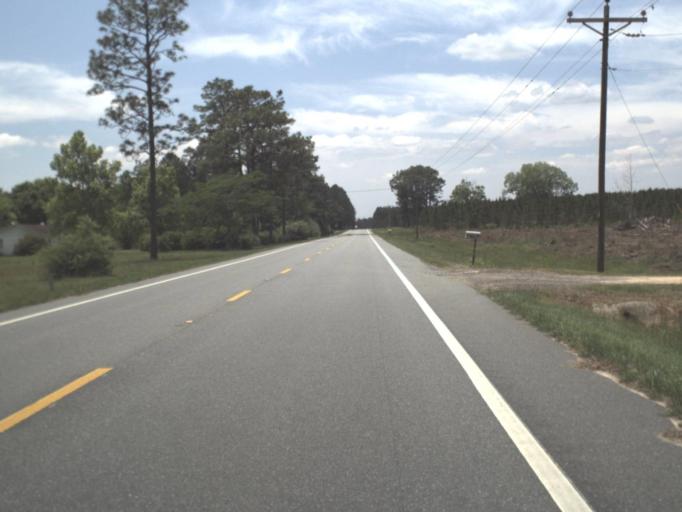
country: US
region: Florida
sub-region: Gulf County
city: Wewahitchka
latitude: 30.2624
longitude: -85.1871
